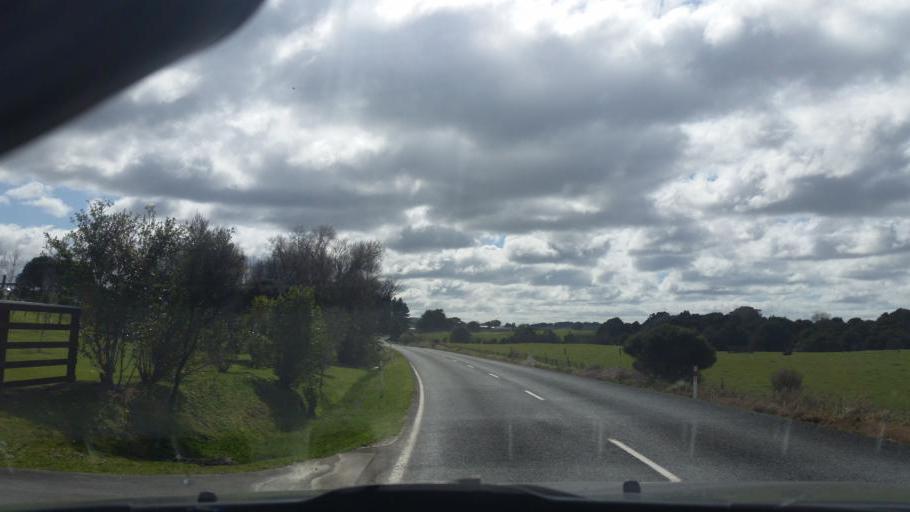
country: NZ
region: Auckland
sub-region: Auckland
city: Wellsford
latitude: -36.1513
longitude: 174.5023
